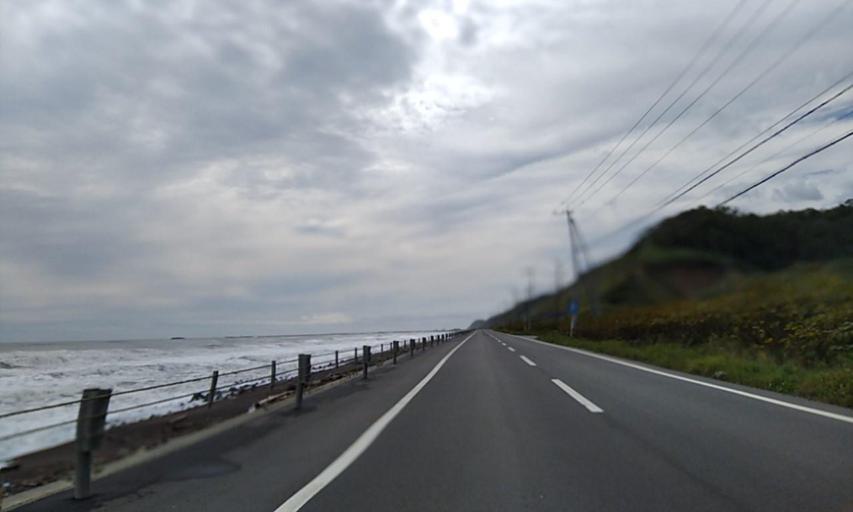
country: JP
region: Hokkaido
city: Kushiro
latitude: 42.8188
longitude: 143.8354
